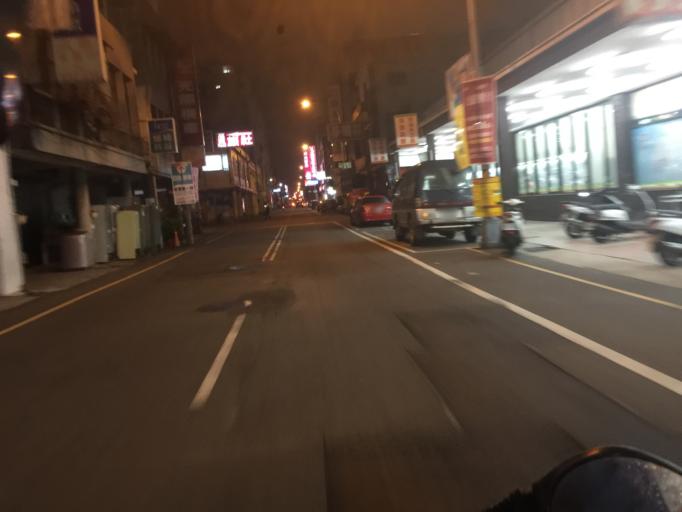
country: TW
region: Taiwan
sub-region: Miaoli
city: Miaoli
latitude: 24.5678
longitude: 120.8236
